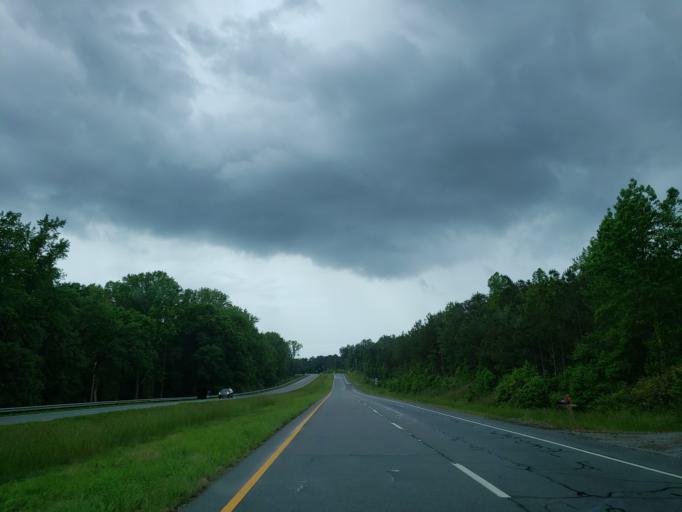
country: US
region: Georgia
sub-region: Haralson County
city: Buchanan
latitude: 33.8377
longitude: -85.2093
